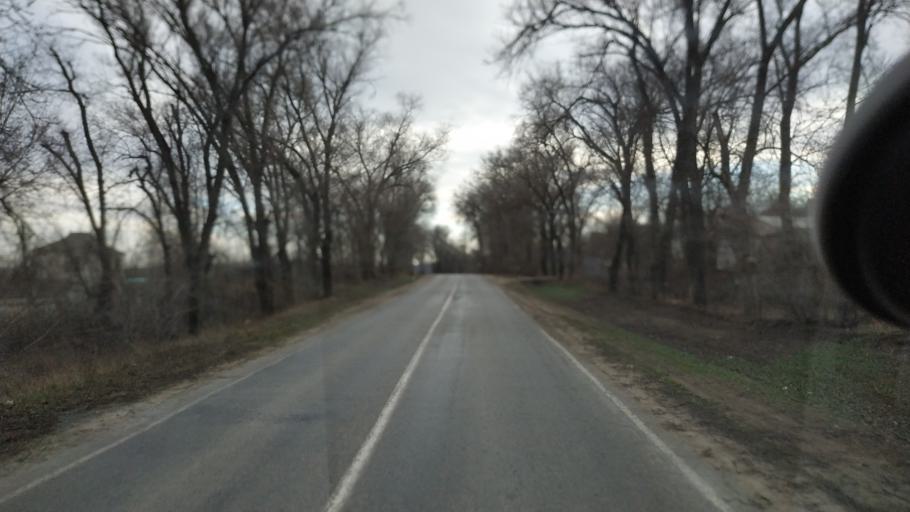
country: MD
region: Chisinau
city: Vadul lui Voda
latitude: 47.1233
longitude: 29.0638
